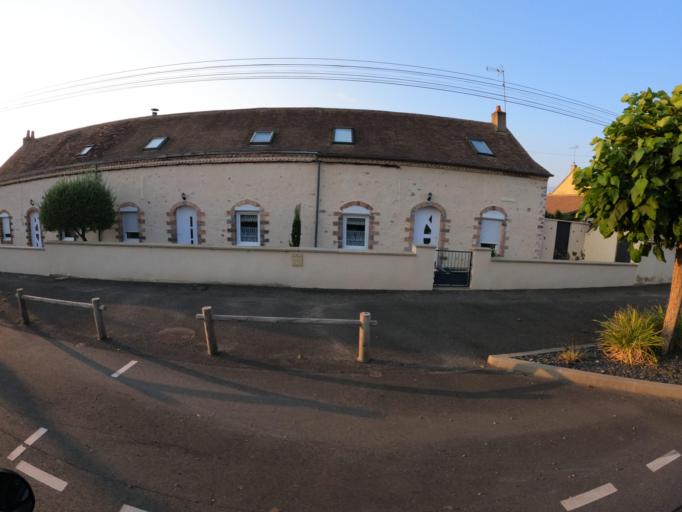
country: FR
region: Pays de la Loire
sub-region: Departement de la Sarthe
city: Auvers-le-Hamon
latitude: 47.8674
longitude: -0.4281
